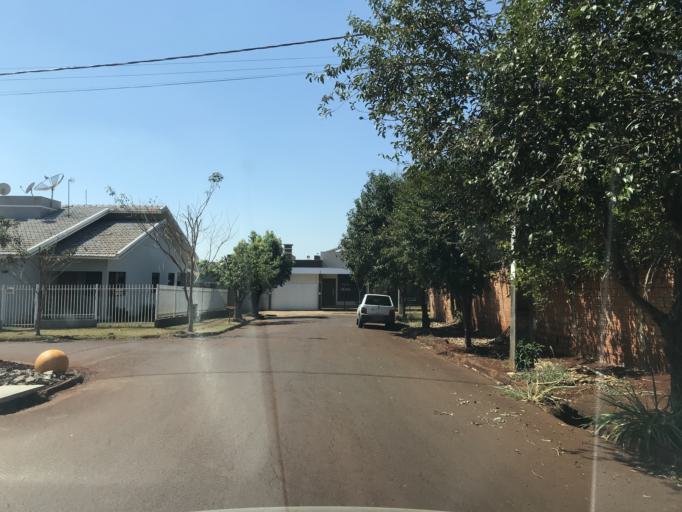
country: BR
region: Parana
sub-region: Palotina
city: Palotina
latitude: -24.2932
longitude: -53.8357
